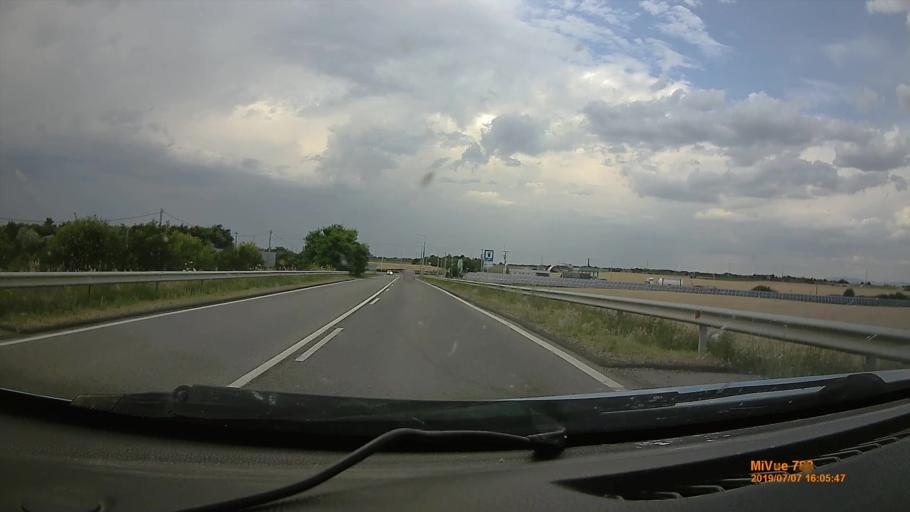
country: HU
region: Heves
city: Hatvan
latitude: 47.6665
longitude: 19.7212
